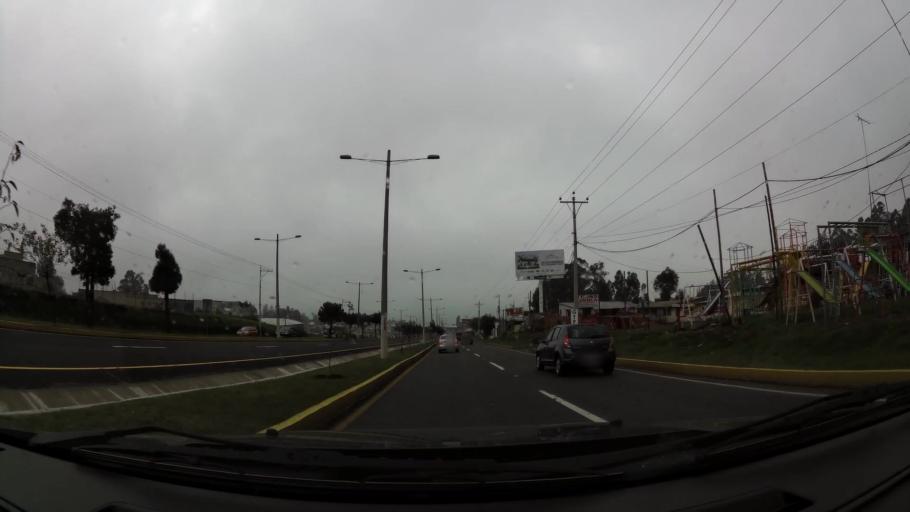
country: EC
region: Pichincha
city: Quito
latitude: -0.2772
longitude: -78.4856
